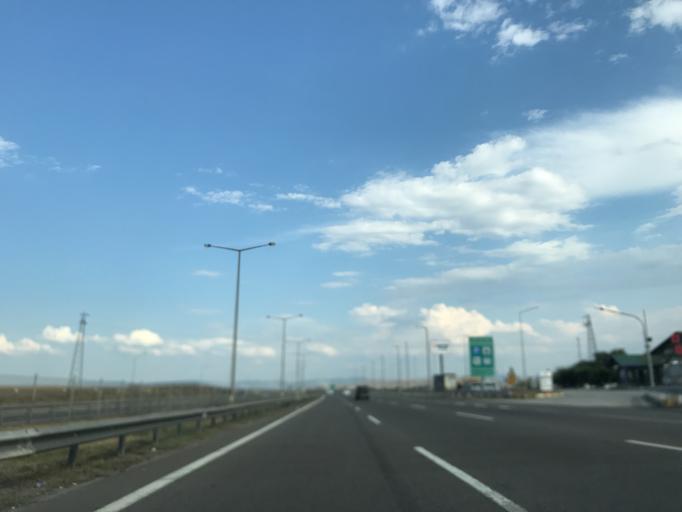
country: TR
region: Bolu
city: Dortdivan
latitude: 40.7499
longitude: 32.0831
